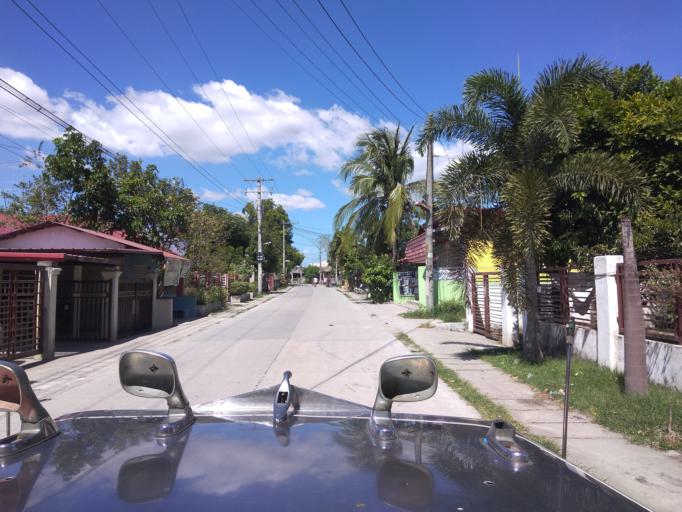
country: PH
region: Central Luzon
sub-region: Province of Pampanga
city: Magliman
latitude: 15.0411
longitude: 120.6450
